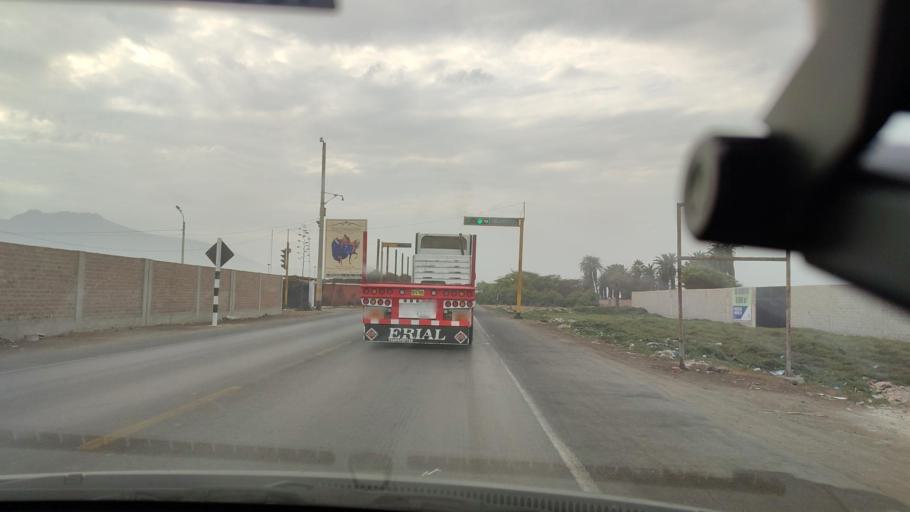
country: PE
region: La Libertad
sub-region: Provincia de Trujillo
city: Buenos Aires
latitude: -8.1505
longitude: -79.0411
